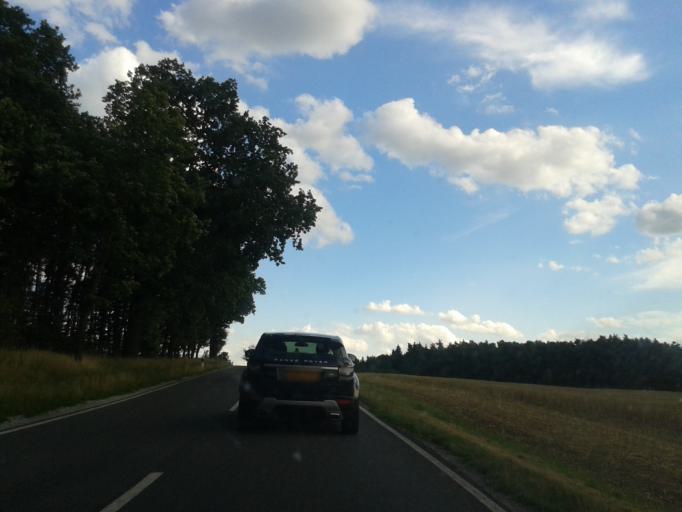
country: DE
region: Saxony
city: Radeberg
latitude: 51.0678
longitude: 13.9333
